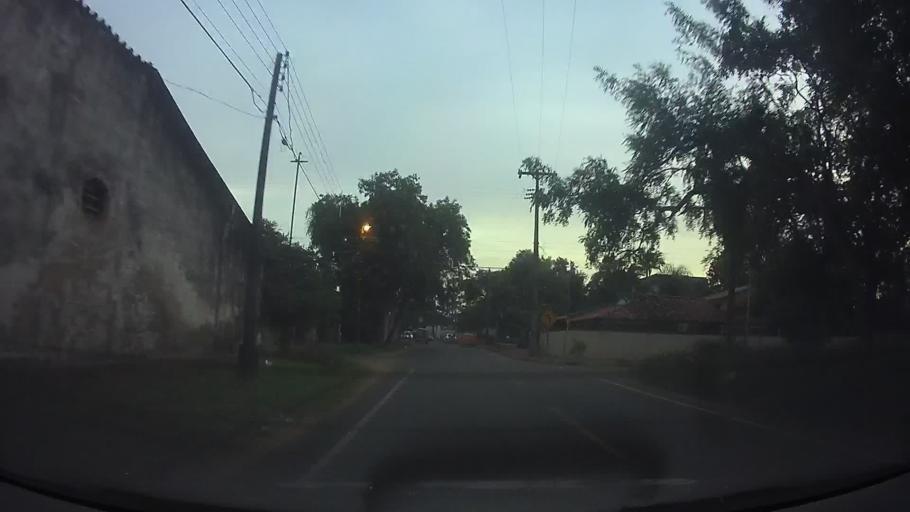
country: PY
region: Central
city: San Lorenzo
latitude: -25.2580
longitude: -57.5032
